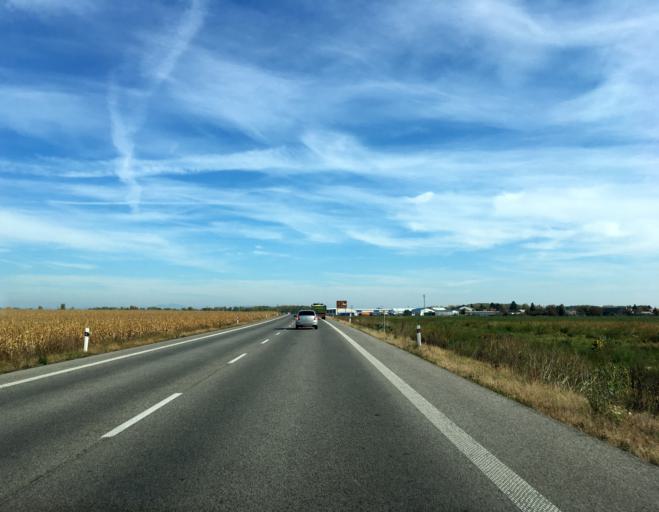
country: SK
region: Nitriansky
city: Zeliezovce
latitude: 48.1084
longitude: 18.6171
